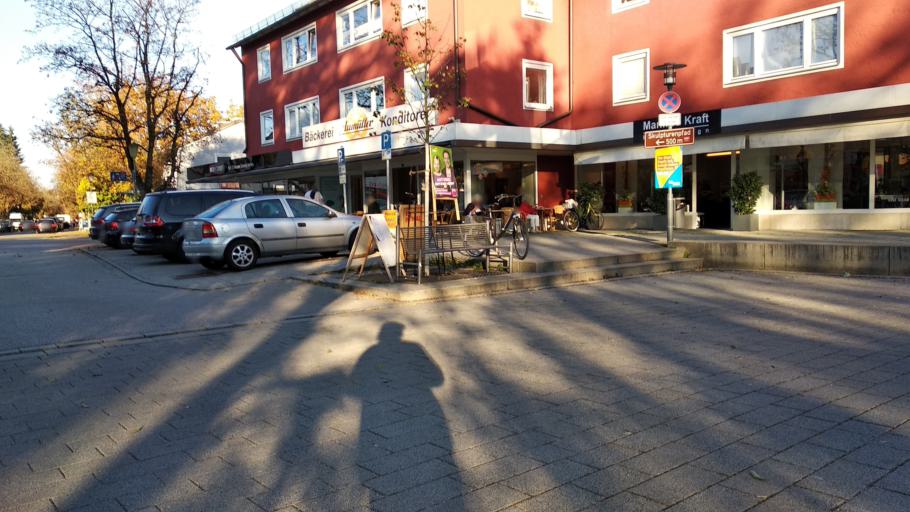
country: DE
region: Bavaria
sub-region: Upper Bavaria
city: Vaterstetten
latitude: 48.1045
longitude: 11.7656
